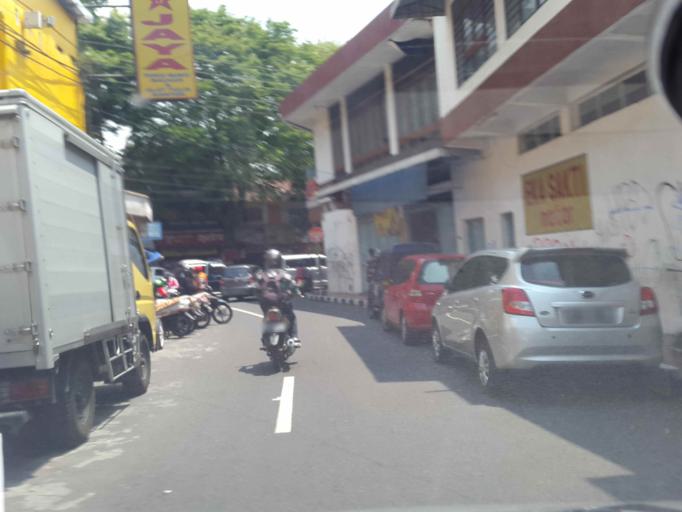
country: ID
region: Central Java
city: Magelang
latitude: -7.4841
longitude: 110.2204
